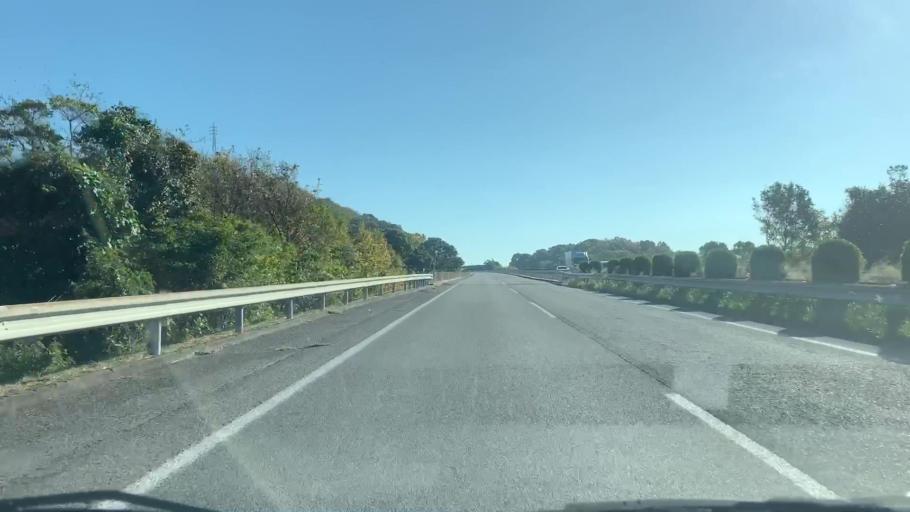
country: JP
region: Saga Prefecture
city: Saga-shi
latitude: 33.2876
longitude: 130.1469
